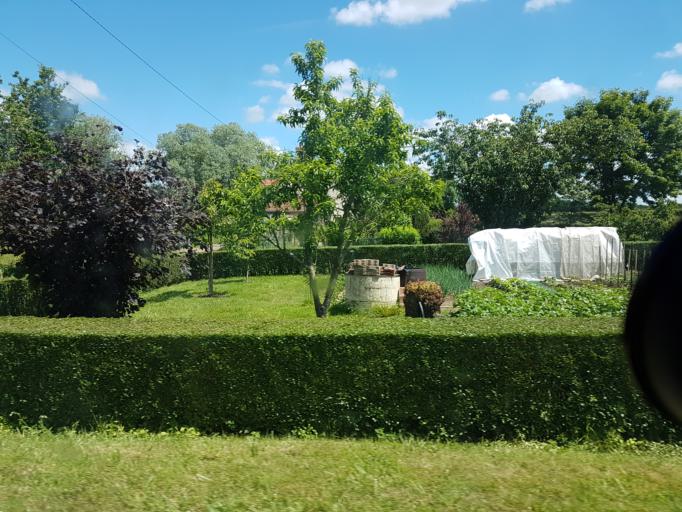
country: FR
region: Bourgogne
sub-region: Departement de Saone-et-Loire
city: Curgy
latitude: 47.0361
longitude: 4.4086
